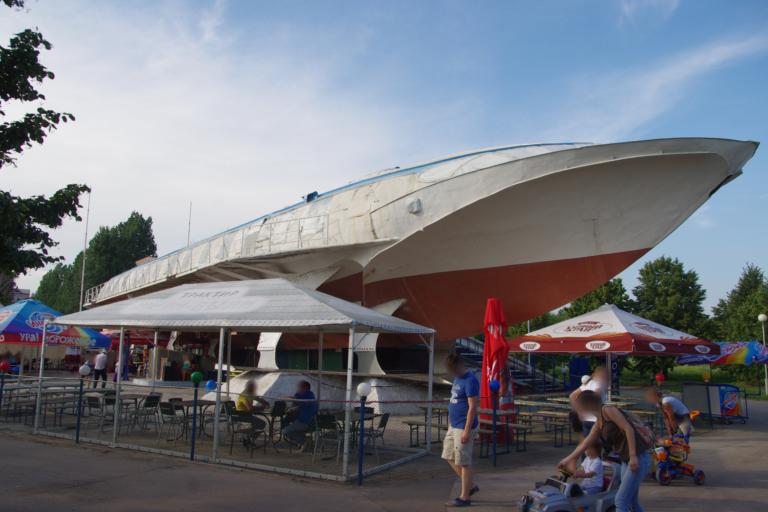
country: RU
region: Samara
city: Zhigulevsk
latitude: 53.4719
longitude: 49.4754
